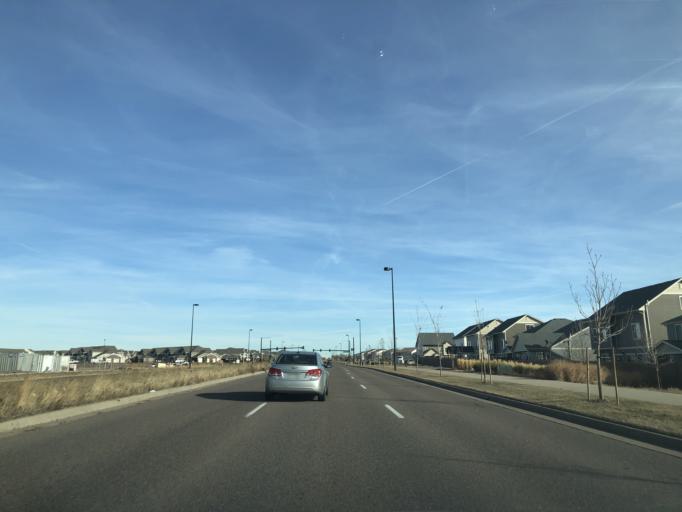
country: US
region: Colorado
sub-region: Adams County
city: Aurora
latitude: 39.7983
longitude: -104.7658
